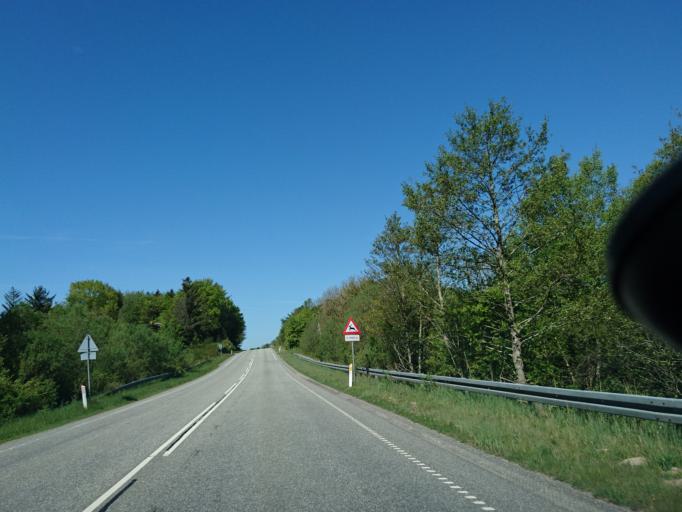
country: DK
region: North Denmark
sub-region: Hjorring Kommune
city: Sindal
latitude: 57.4645
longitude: 10.2797
